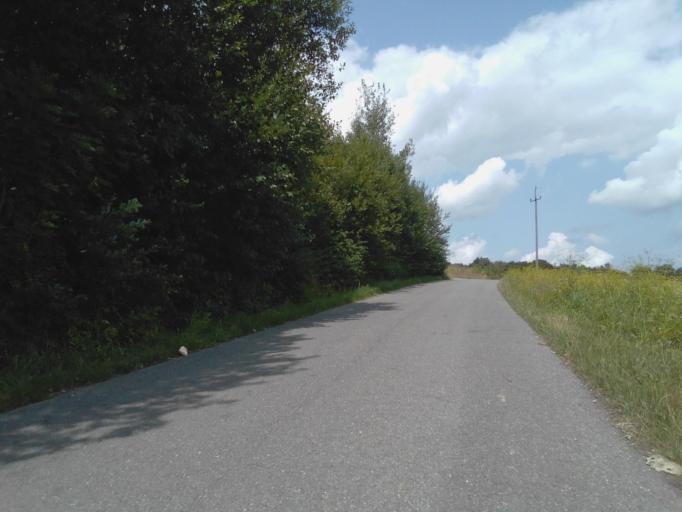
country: PL
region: Subcarpathian Voivodeship
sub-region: Powiat strzyzowski
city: Frysztak
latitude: 49.8207
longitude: 21.5948
